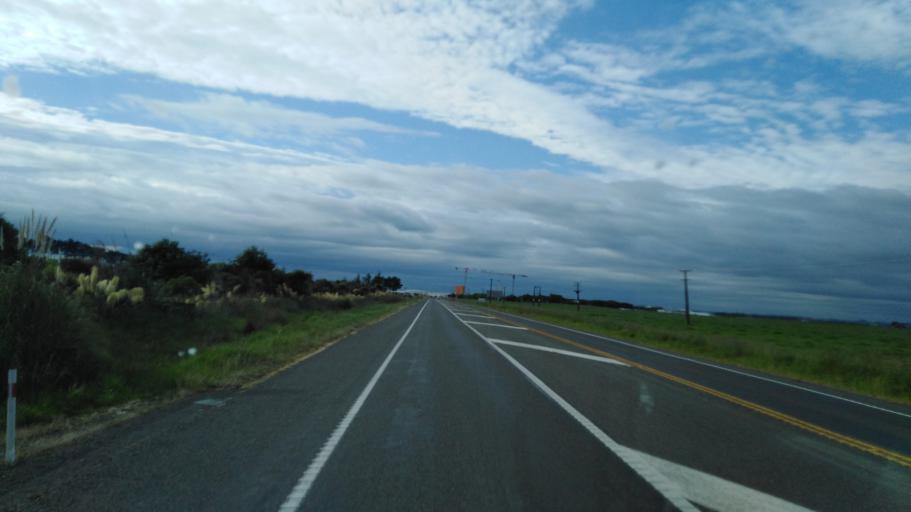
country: NZ
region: Manawatu-Wanganui
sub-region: Rangitikei District
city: Bulls
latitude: -40.1941
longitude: 175.3901
